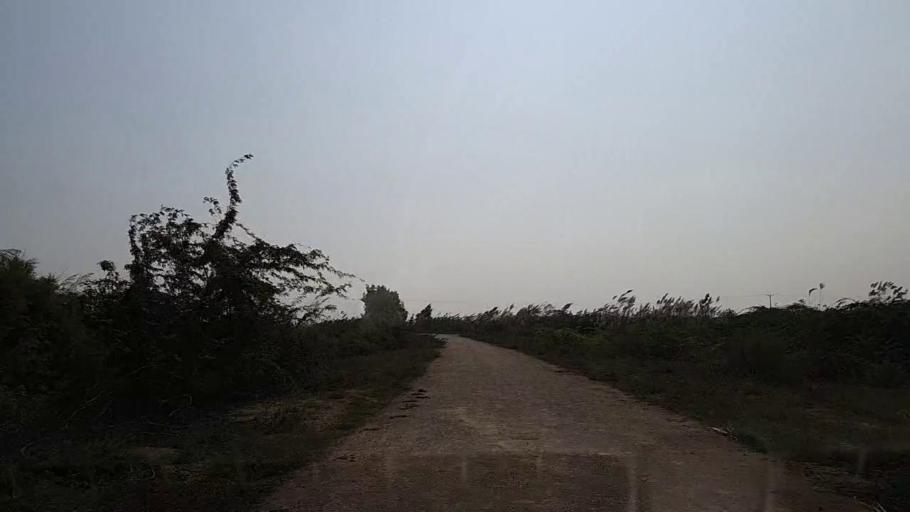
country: PK
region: Sindh
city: Mirpur Sakro
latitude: 24.6518
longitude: 67.6903
